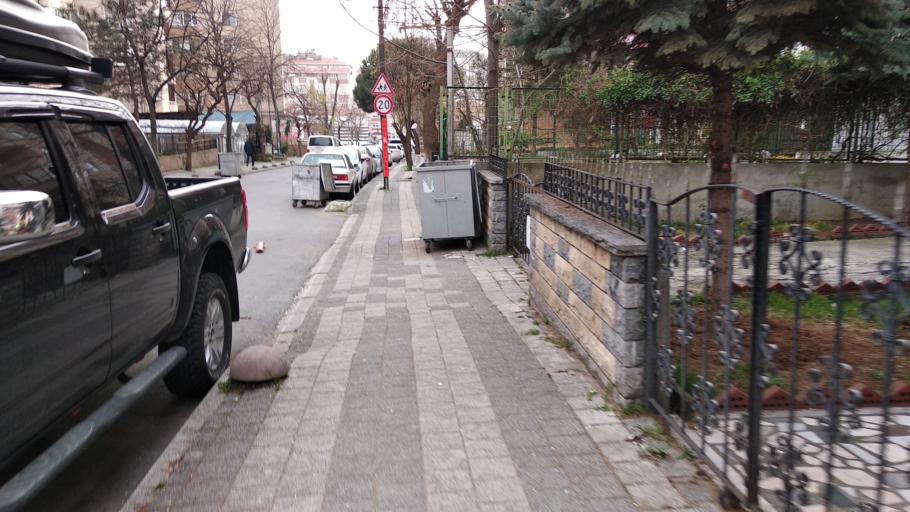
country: TR
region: Istanbul
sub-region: Atasehir
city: Atasehir
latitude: 40.9723
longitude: 29.1120
